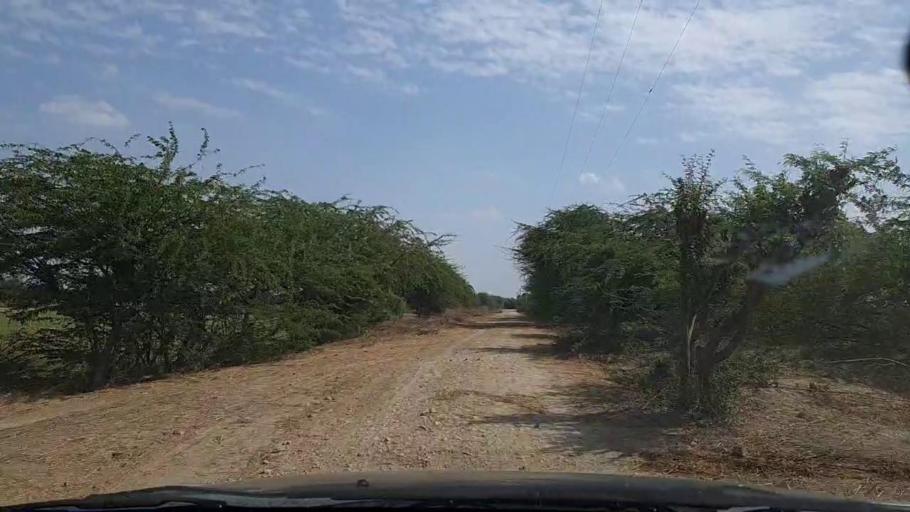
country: PK
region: Sindh
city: Mirpur Batoro
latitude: 24.5653
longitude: 68.1994
